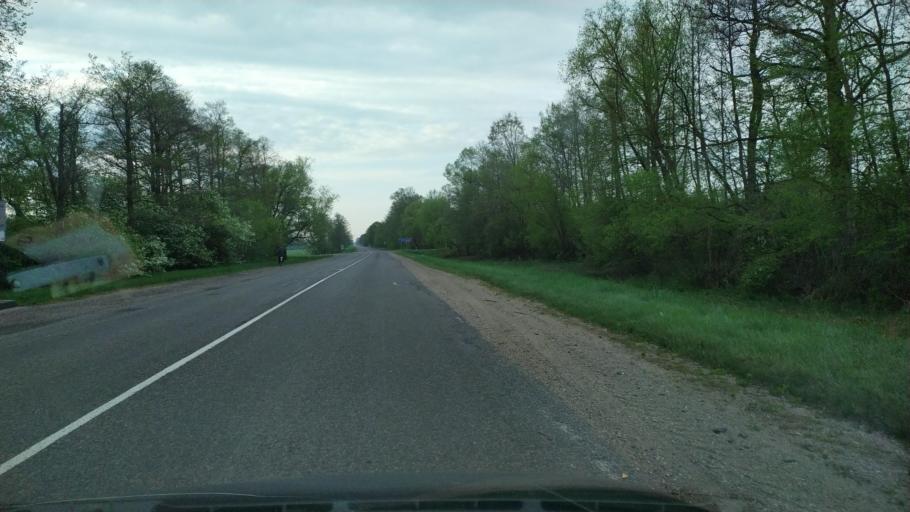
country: BY
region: Brest
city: Zhabinka
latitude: 52.2389
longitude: 23.9783
